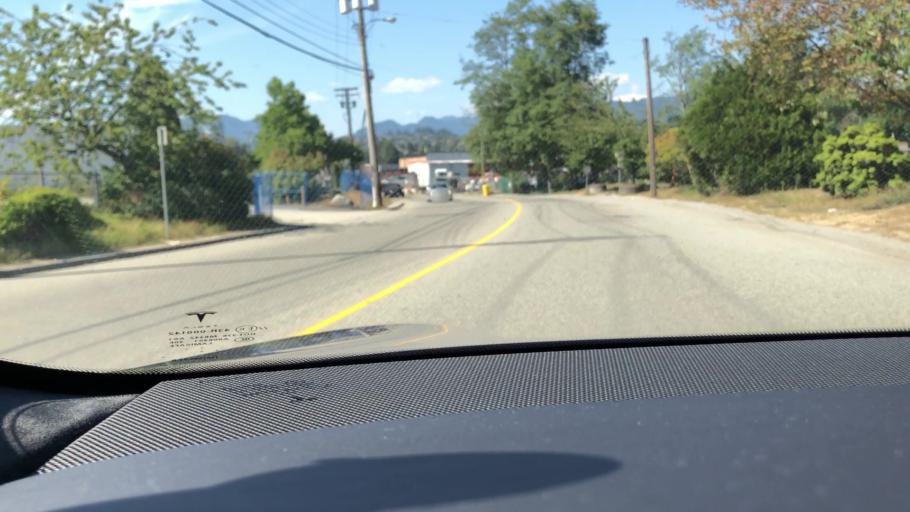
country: CA
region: British Columbia
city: Burnaby
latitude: 49.2540
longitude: -122.9751
